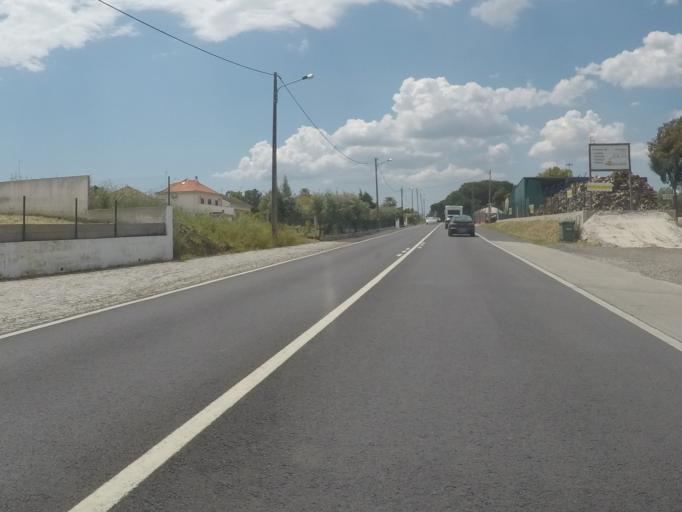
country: PT
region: Setubal
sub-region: Setubal
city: Setubal
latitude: 38.5457
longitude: -8.8201
